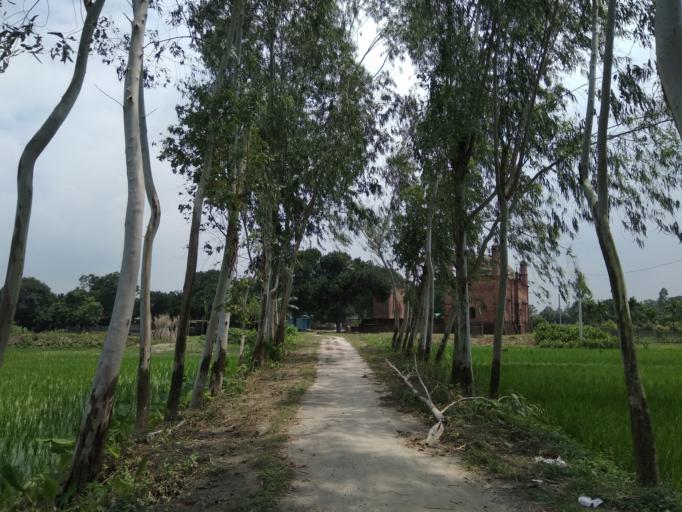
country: BD
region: Rangpur Division
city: Thakurgaon
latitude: 26.1259
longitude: 88.5637
